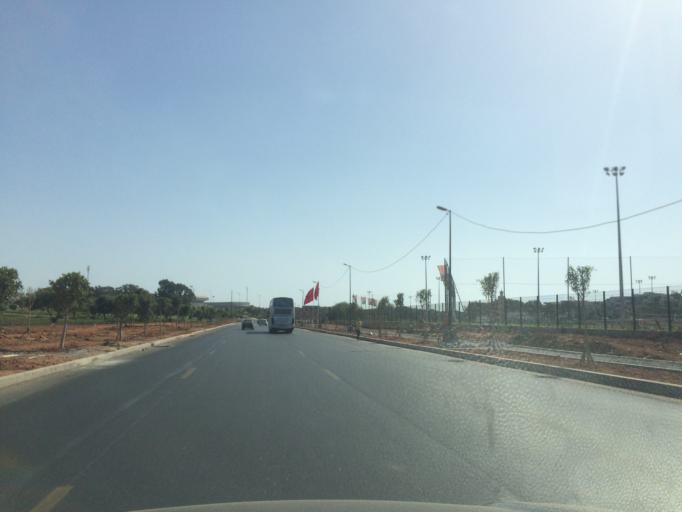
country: MA
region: Rabat-Sale-Zemmour-Zaer
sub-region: Skhirate-Temara
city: Temara
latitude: 33.9711
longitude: -6.8815
